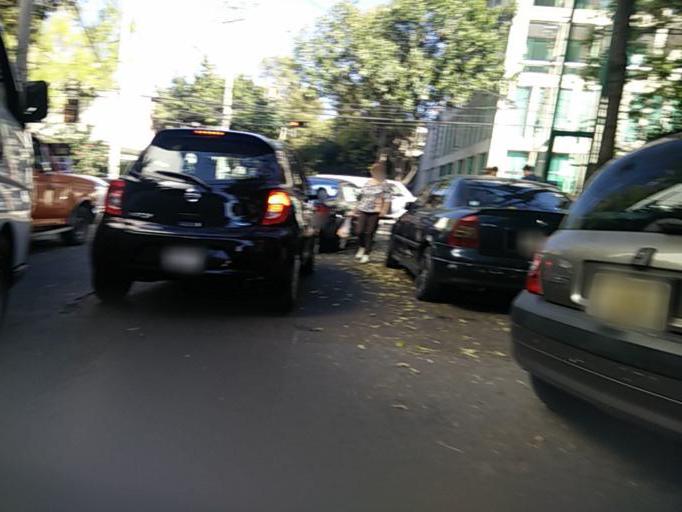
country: MX
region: Mexico City
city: Benito Juarez
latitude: 19.4120
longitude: -99.1648
